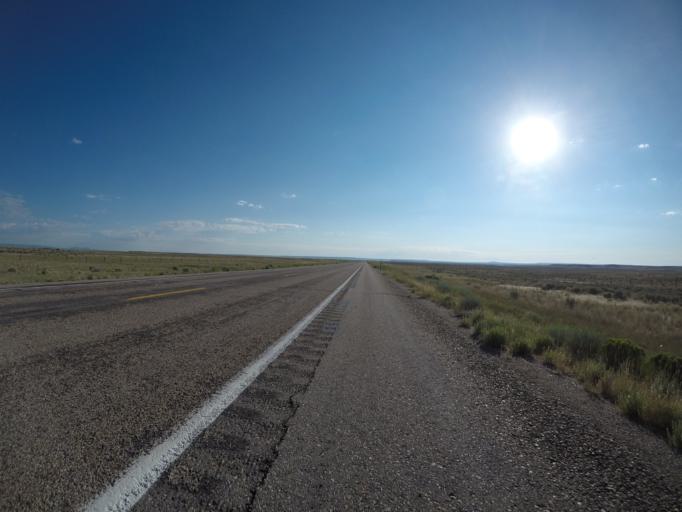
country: US
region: Wyoming
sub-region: Lincoln County
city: Kemmerer
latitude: 41.9252
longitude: -110.2836
